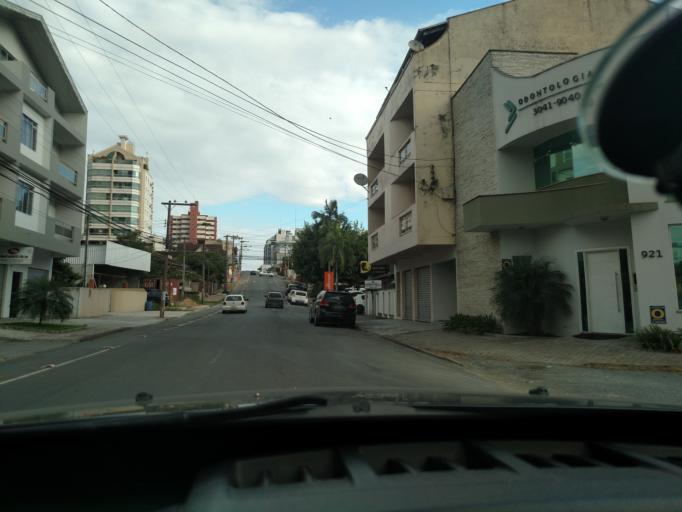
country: BR
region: Santa Catarina
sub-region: Blumenau
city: Blumenau
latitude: -26.9035
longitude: -49.0888
